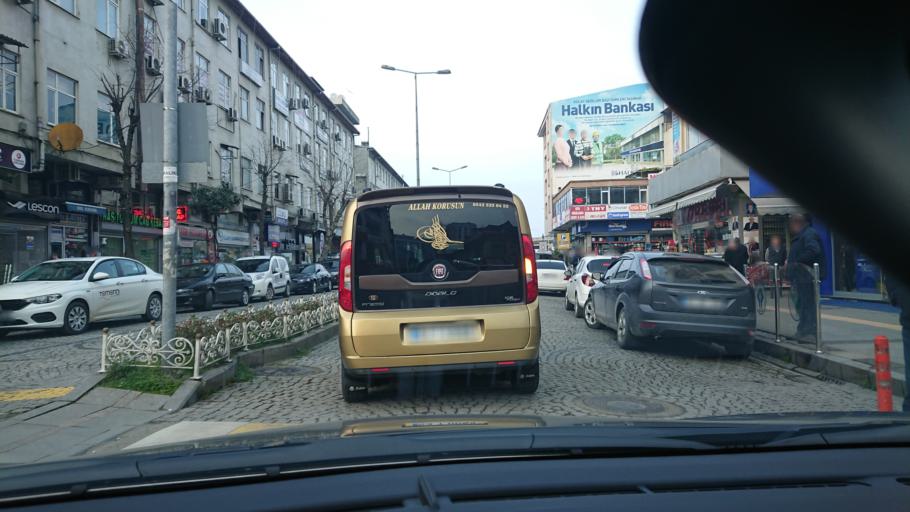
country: TR
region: Rize
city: Rize
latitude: 41.0256
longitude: 40.5178
